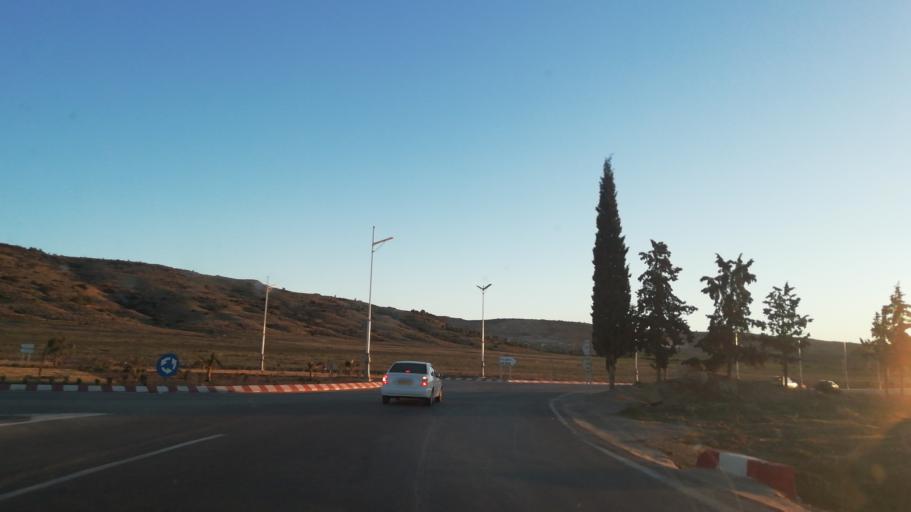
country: DZ
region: Saida
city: Saida
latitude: 34.8529
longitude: 0.1966
